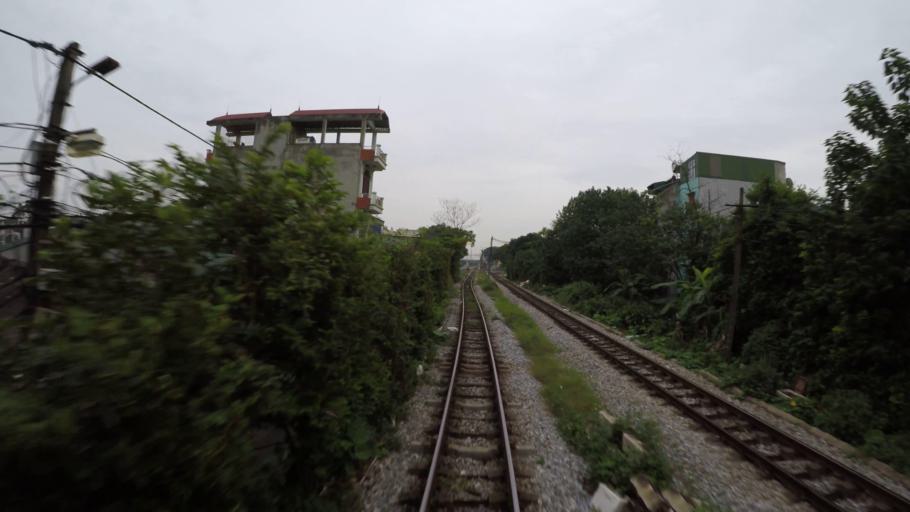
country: VN
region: Ha Noi
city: Trau Quy
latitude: 21.0357
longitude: 105.9016
